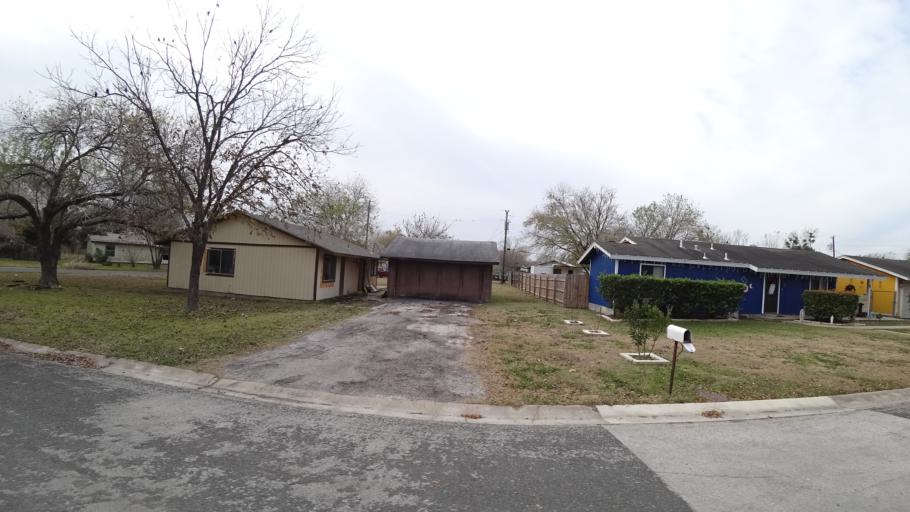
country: US
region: Texas
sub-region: Travis County
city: Onion Creek
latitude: 30.1354
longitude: -97.6771
